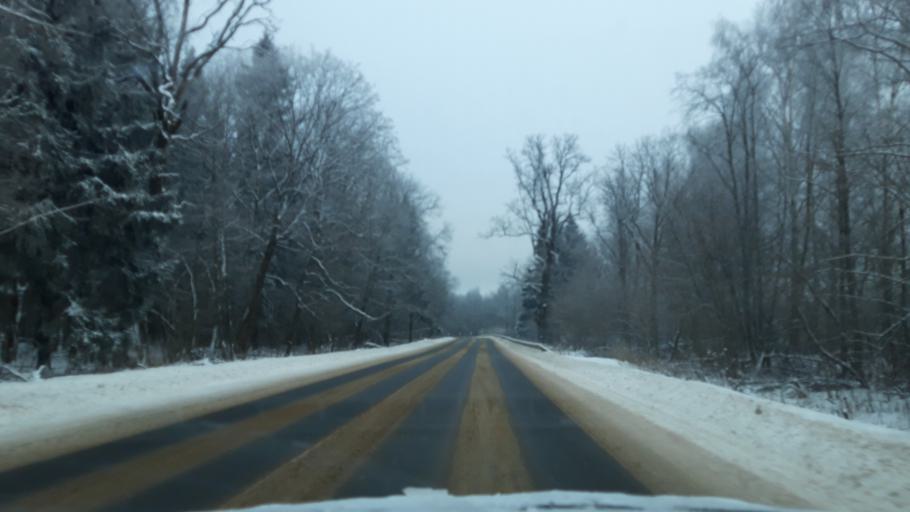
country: RU
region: Moskovskaya
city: Avtopoligon
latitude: 56.2789
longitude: 37.3727
